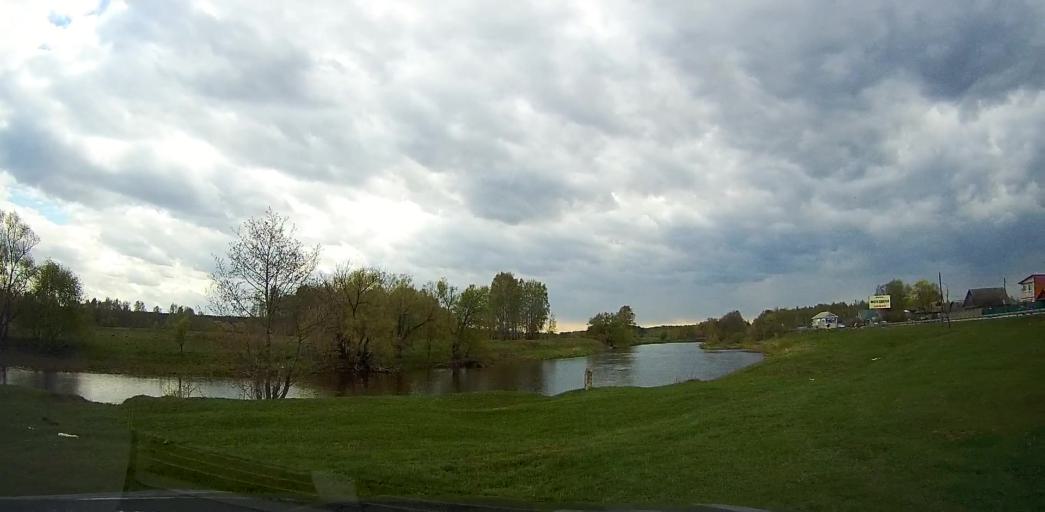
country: RU
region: Moskovskaya
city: Pavlovskiy Posad
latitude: 55.8021
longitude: 38.6713
